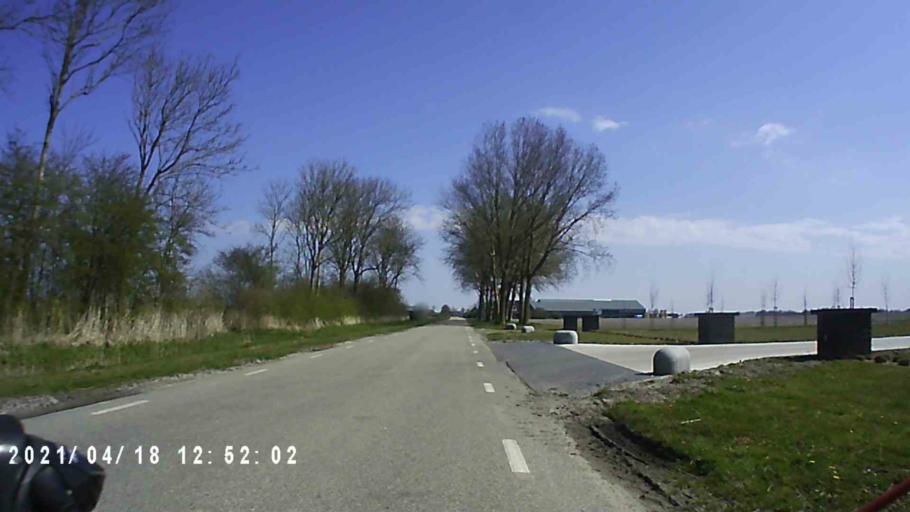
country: NL
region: Friesland
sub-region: Gemeente Dongeradeel
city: Anjum
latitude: 53.3808
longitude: 6.0600
